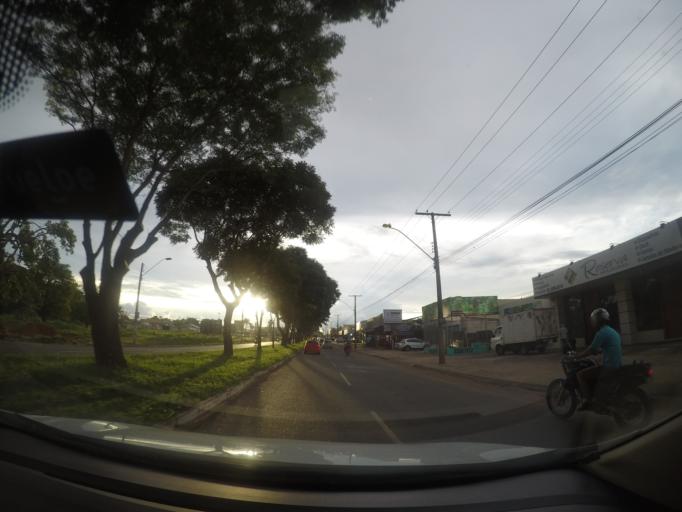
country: BR
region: Goias
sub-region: Goiania
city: Goiania
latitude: -16.7496
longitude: -49.3288
